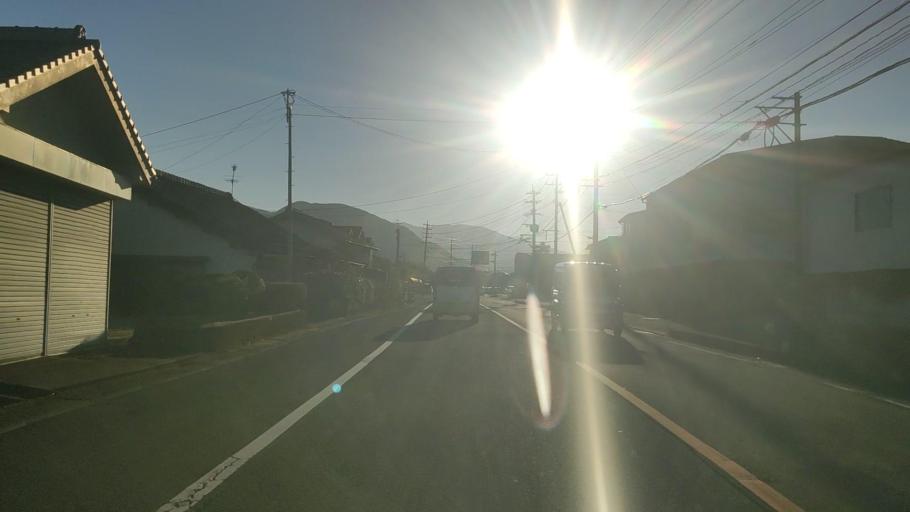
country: JP
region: Miyazaki
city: Miyazaki-shi
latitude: 31.8487
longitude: 131.3506
